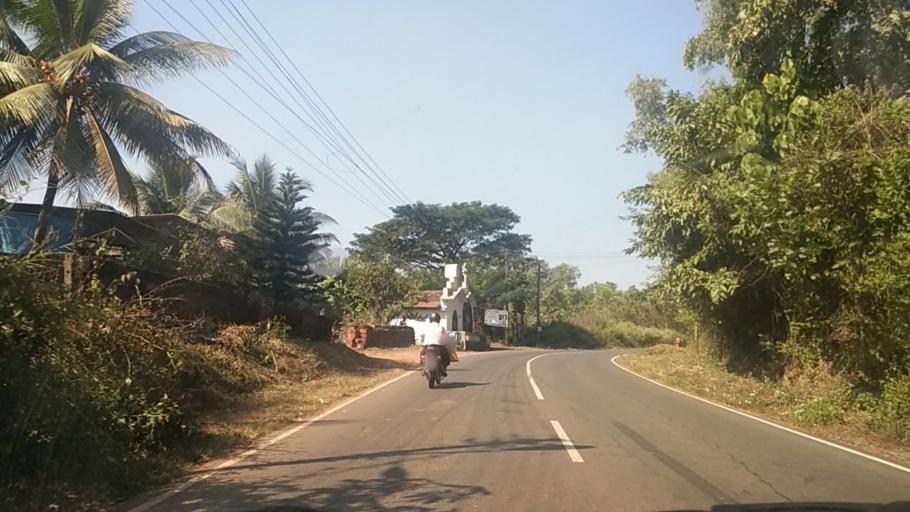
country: IN
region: Goa
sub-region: South Goa
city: Sanguem
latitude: 15.2298
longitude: 74.1338
